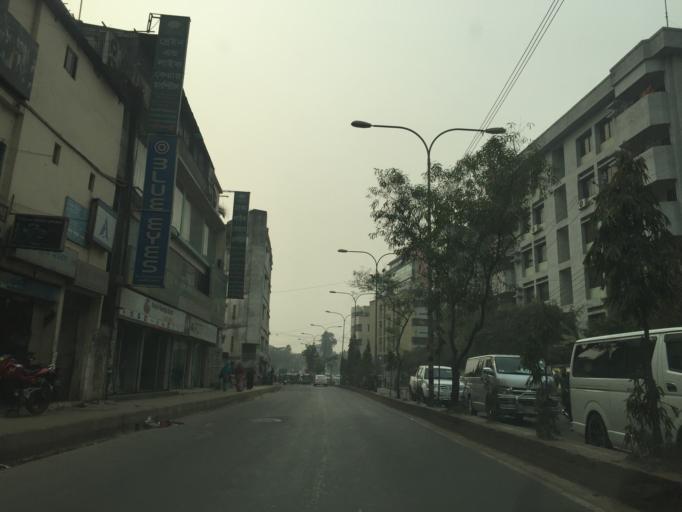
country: BD
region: Dhaka
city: Azimpur
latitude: 23.7645
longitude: 90.3911
